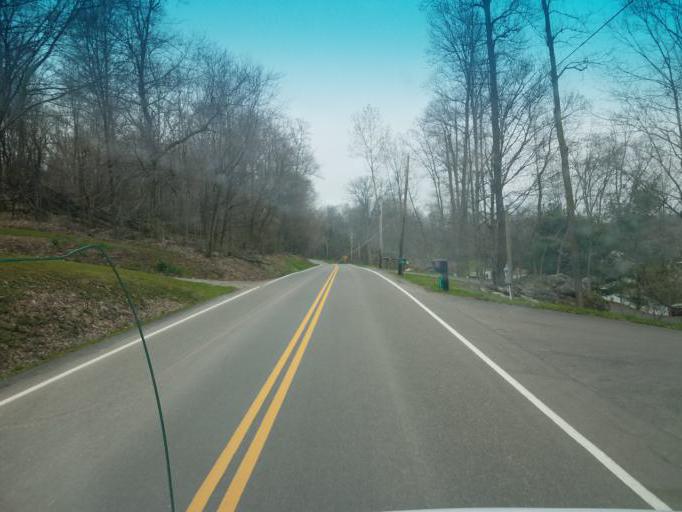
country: US
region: Ohio
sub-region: Stark County
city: Beach City
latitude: 40.6112
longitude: -81.6759
